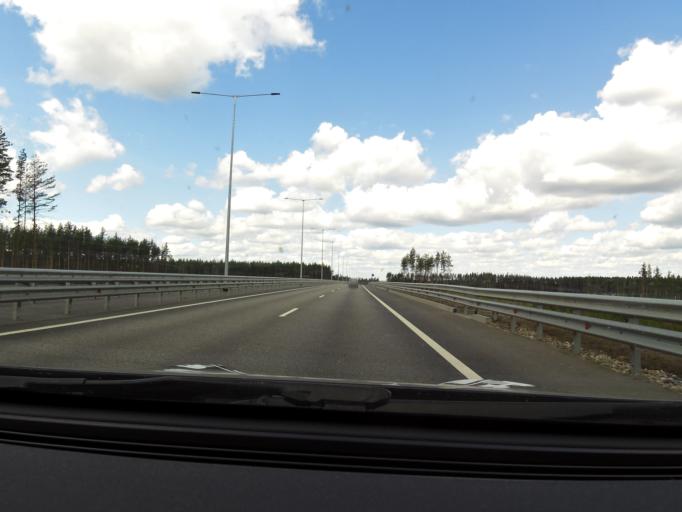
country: RU
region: Tverskaya
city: Krasnomayskiy
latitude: 57.4775
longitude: 34.3354
